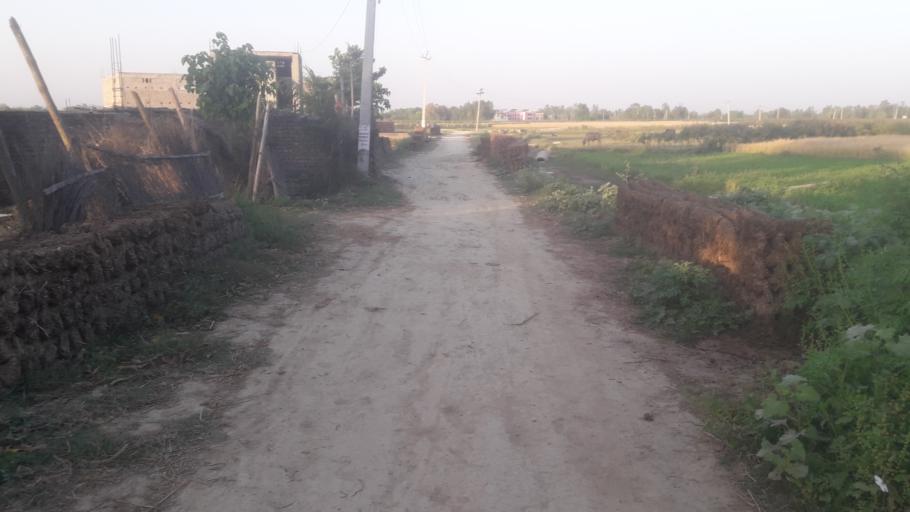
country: NP
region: Eastern Region
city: Siraha
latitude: 26.6307
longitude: 86.1926
